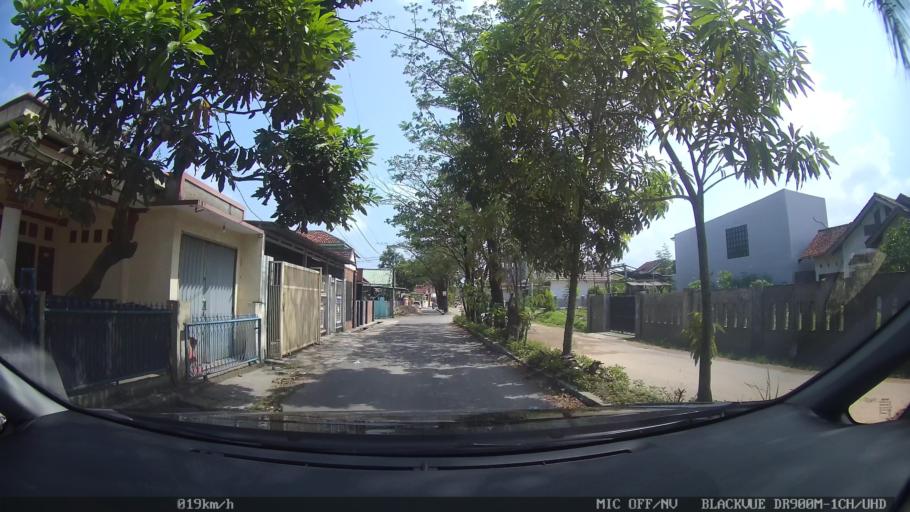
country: ID
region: Lampung
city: Kedaton
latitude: -5.3604
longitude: 105.2810
